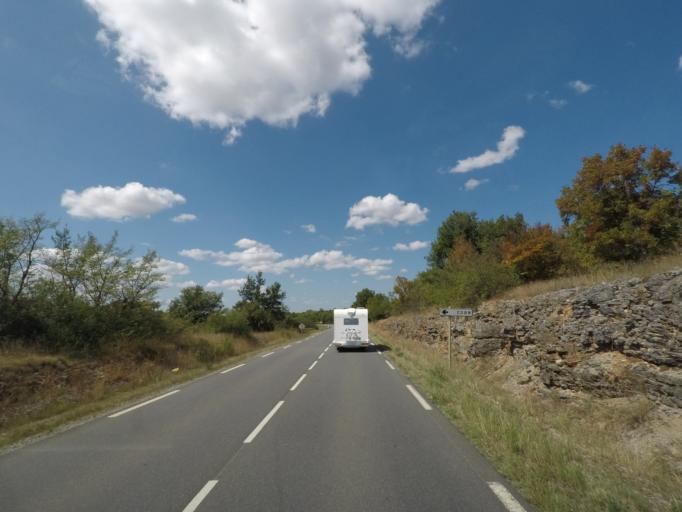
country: FR
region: Midi-Pyrenees
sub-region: Departement du Lot
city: Lacapelle-Marival
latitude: 44.6256
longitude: 1.8912
